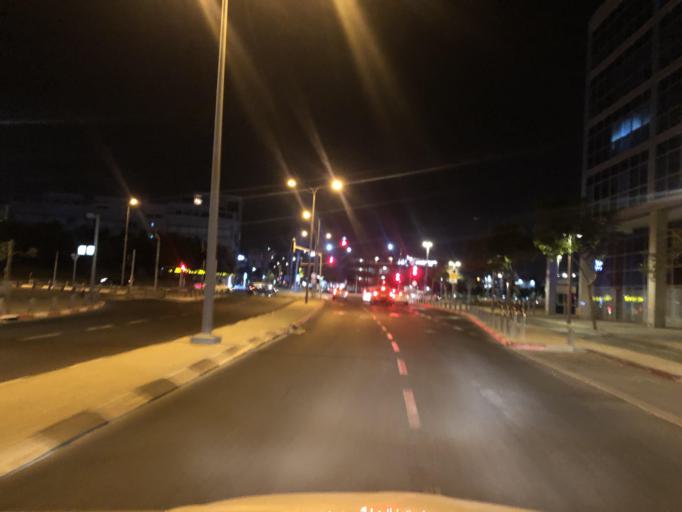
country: IL
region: Tel Aviv
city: Yafo
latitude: 32.0531
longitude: 34.7646
